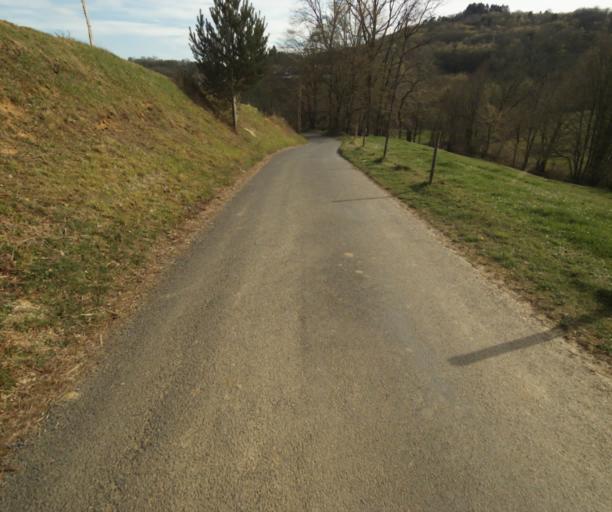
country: FR
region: Limousin
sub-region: Departement de la Correze
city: Naves
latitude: 45.2918
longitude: 1.7592
